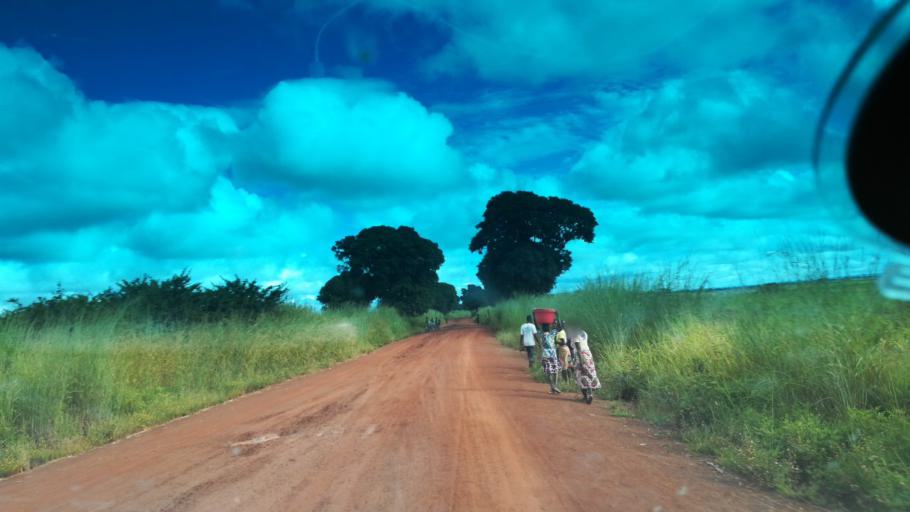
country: ZM
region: Luapula
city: Nchelenge
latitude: -9.2722
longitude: 28.3142
